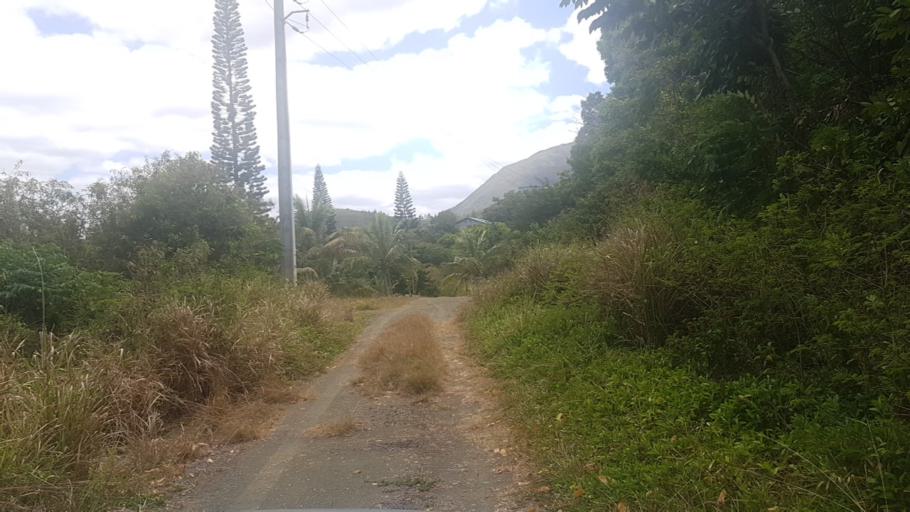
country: NC
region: South Province
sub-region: Dumbea
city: Dumbea
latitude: -22.1844
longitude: 166.4794
